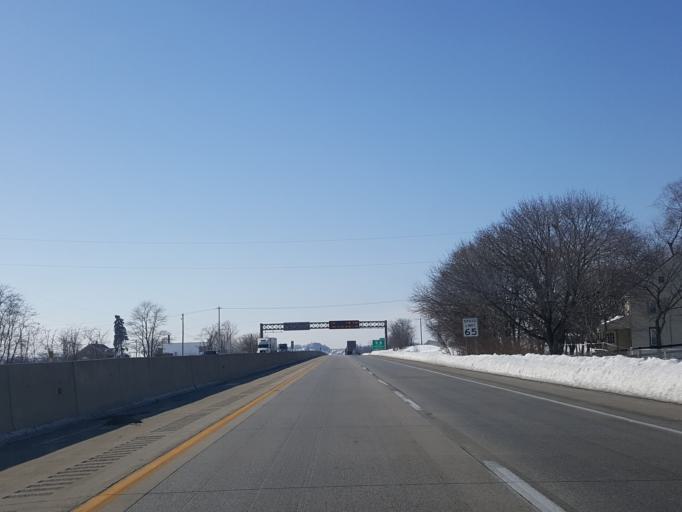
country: US
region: Pennsylvania
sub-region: Lebanon County
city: Fredericksburg
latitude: 40.4641
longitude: -76.3503
